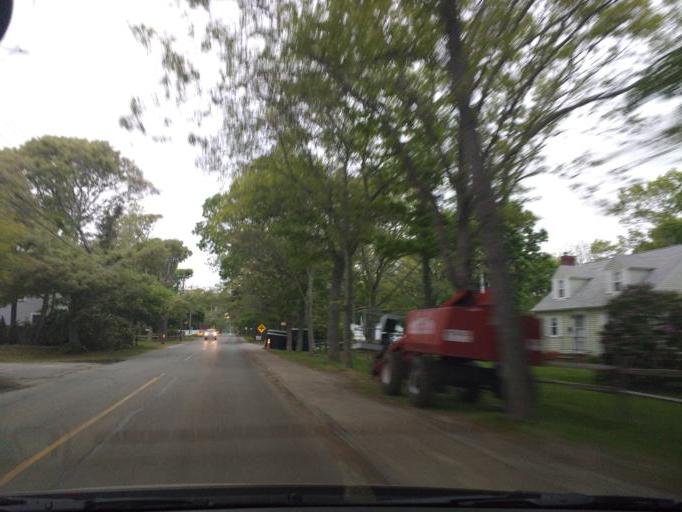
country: US
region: Massachusetts
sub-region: Barnstable County
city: Teaticket
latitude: 41.5624
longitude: -70.5888
